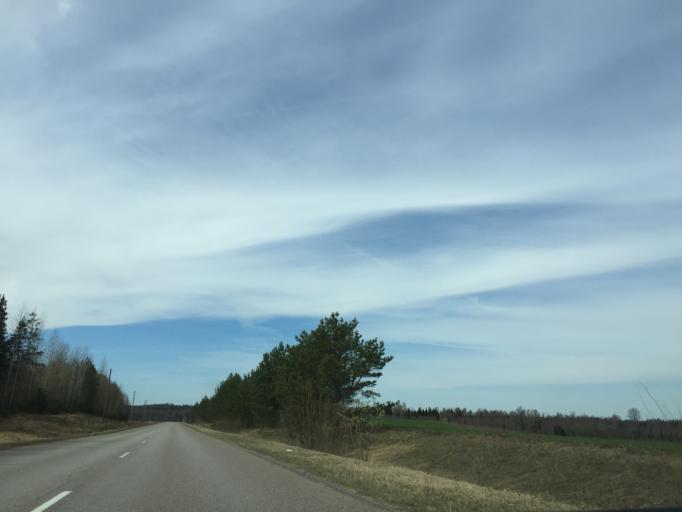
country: LV
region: Valkas Rajons
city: Valka
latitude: 57.7888
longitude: 25.8940
